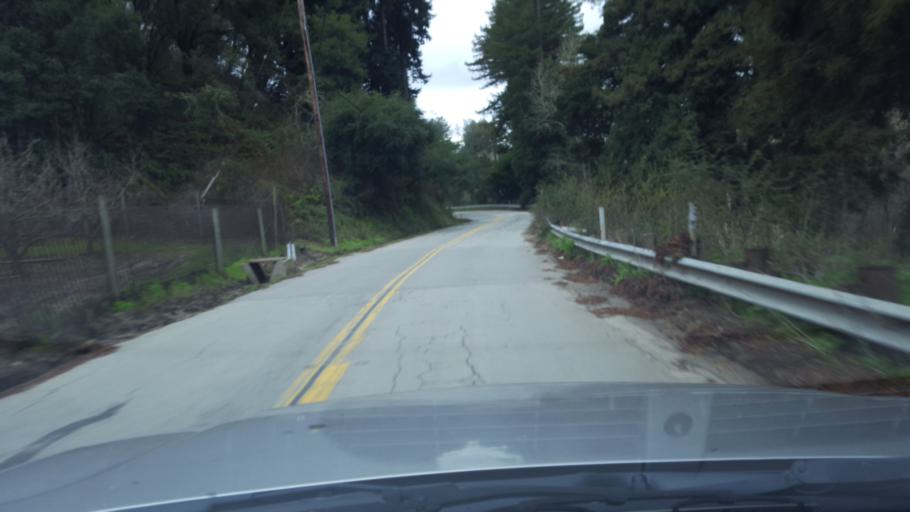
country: US
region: California
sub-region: Santa Cruz County
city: Corralitos
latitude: 37.0010
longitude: -121.7714
